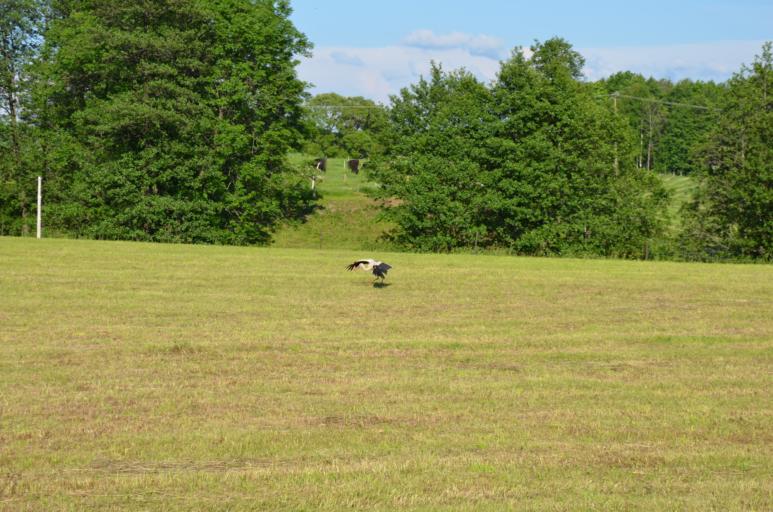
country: PL
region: Podlasie
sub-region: Powiat suwalski
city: Filipow
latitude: 54.3630
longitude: 22.7929
